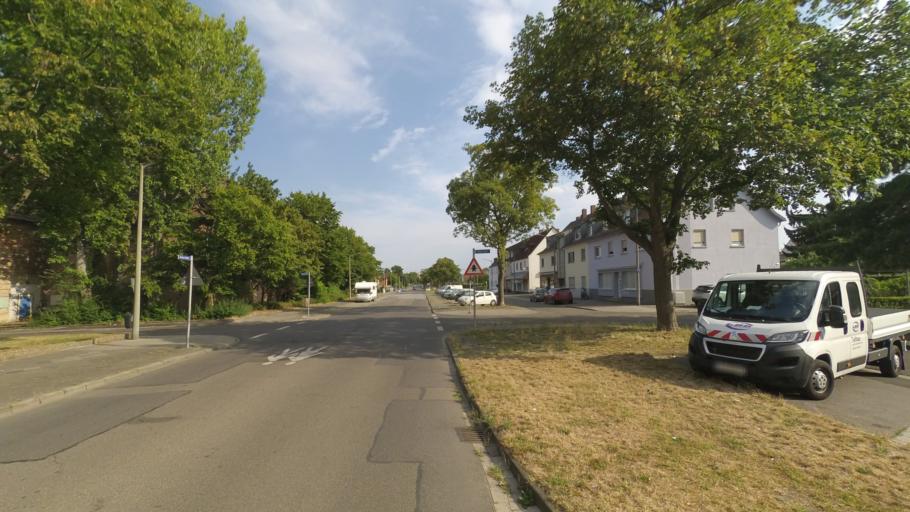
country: DE
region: Rheinland-Pfalz
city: Gartenstadt
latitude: 49.4733
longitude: 8.4034
